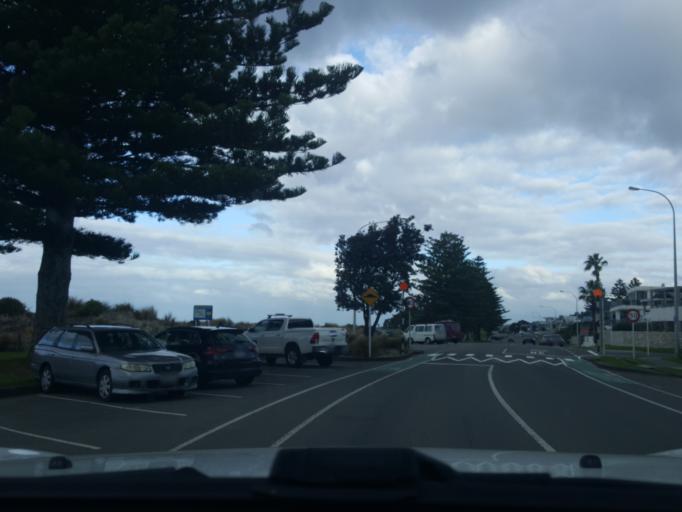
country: NZ
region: Bay of Plenty
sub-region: Tauranga City
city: Tauranga
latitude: -37.6364
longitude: 176.1874
